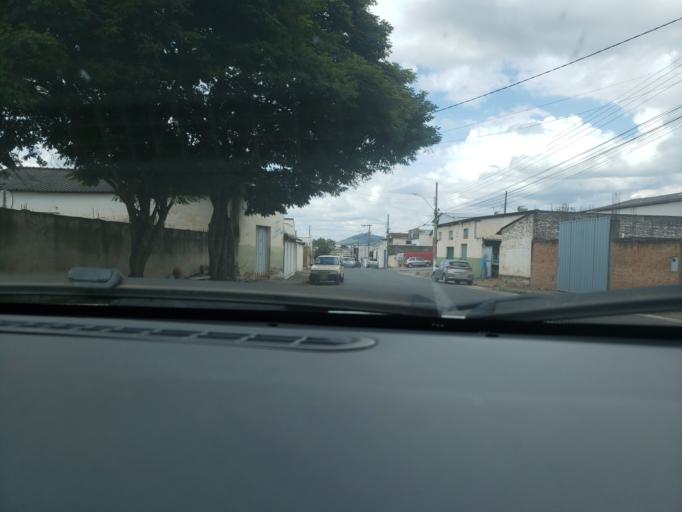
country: BR
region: Minas Gerais
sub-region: Campo Belo
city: Campo Belo
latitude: -20.9054
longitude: -45.2818
